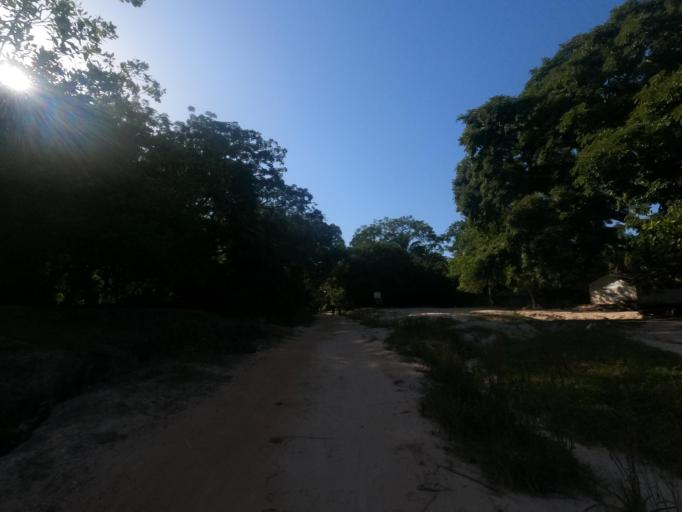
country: GW
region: Cacheu
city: Cacheu
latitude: 12.3937
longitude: -16.2263
